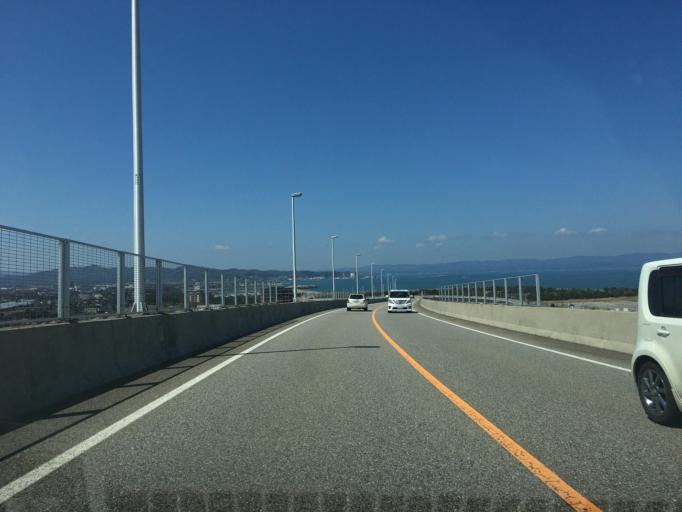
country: JP
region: Toyama
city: Nishishinminato
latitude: 36.7772
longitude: 137.1104
